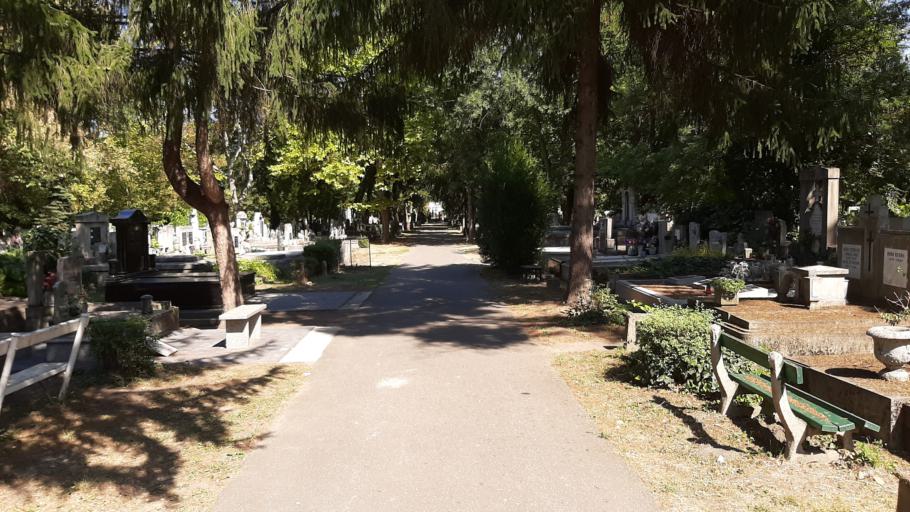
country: HU
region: Csongrad
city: Szeged
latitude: 46.2417
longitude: 20.1283
